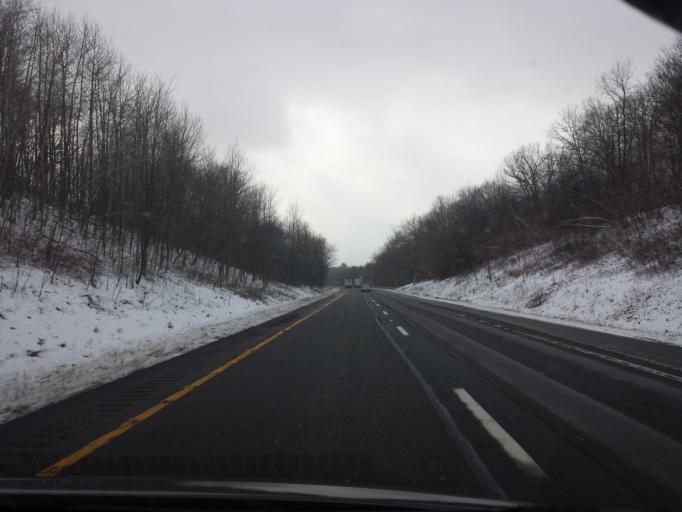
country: US
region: Pennsylvania
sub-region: Luzerne County
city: White Haven
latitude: 41.0759
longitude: -75.6752
